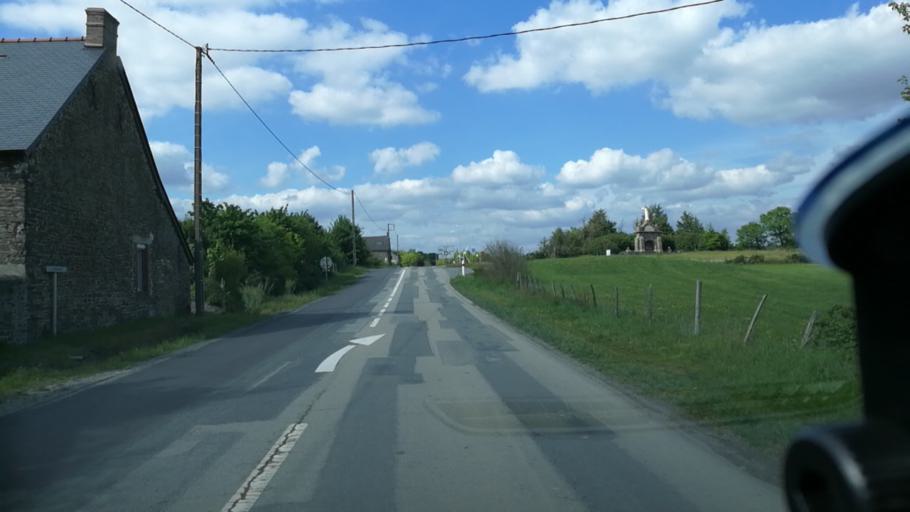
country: FR
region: Brittany
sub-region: Departement d'Ille-et-Vilaine
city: Martigne-Ferchaud
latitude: 47.8385
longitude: -1.3250
